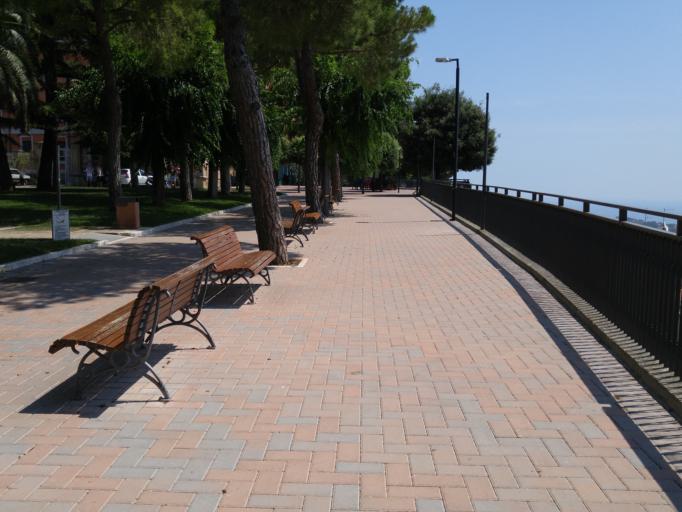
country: IT
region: Abruzzo
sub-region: Provincia di Pescara
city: Citta Sant'Angelo
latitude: 42.5198
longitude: 14.0628
